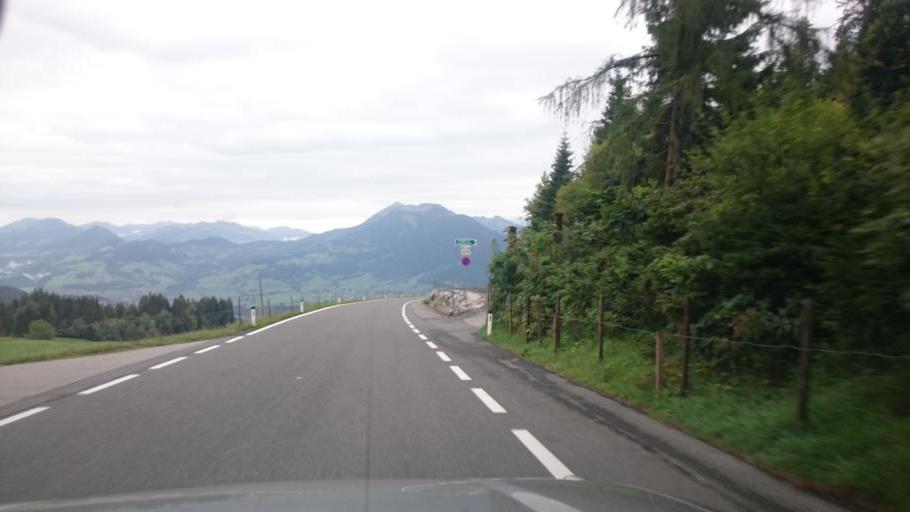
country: AT
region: Vorarlberg
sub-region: Politischer Bezirk Bregenz
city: Bildstein
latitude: 47.4199
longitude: 9.8128
